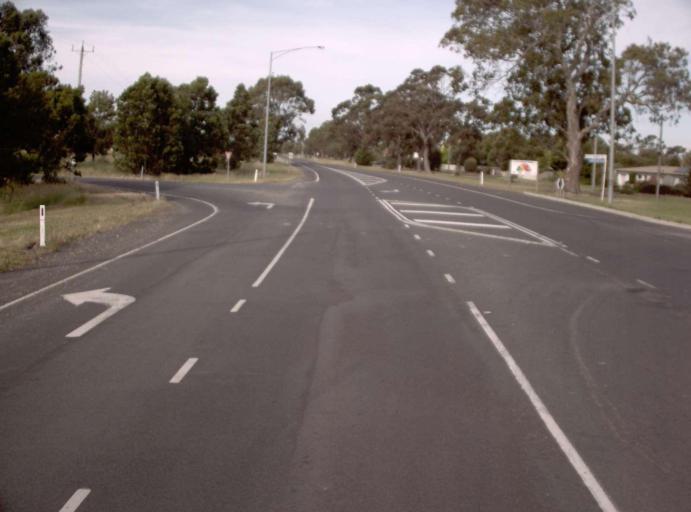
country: AU
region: Victoria
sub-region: Latrobe
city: Traralgon
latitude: -38.1289
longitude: 146.5636
